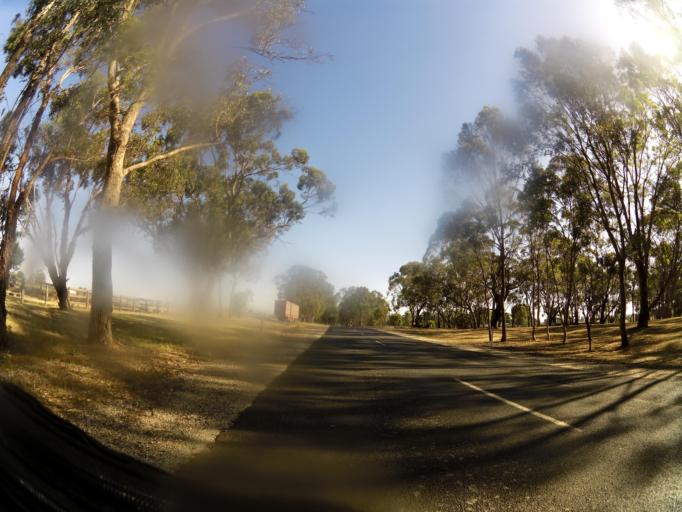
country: AU
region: Victoria
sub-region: Murrindindi
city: Kinglake West
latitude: -36.9621
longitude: 145.1080
